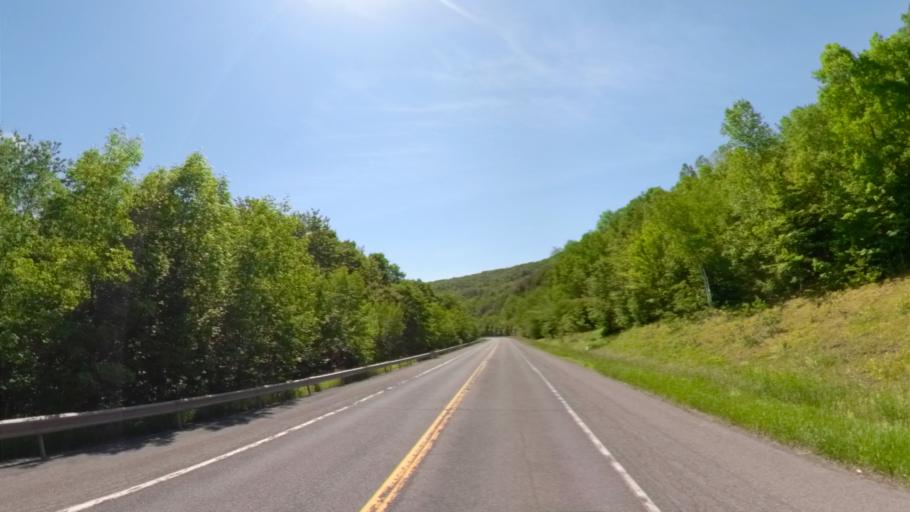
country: US
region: New York
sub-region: Delaware County
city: Stamford
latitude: 42.1524
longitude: -74.5243
